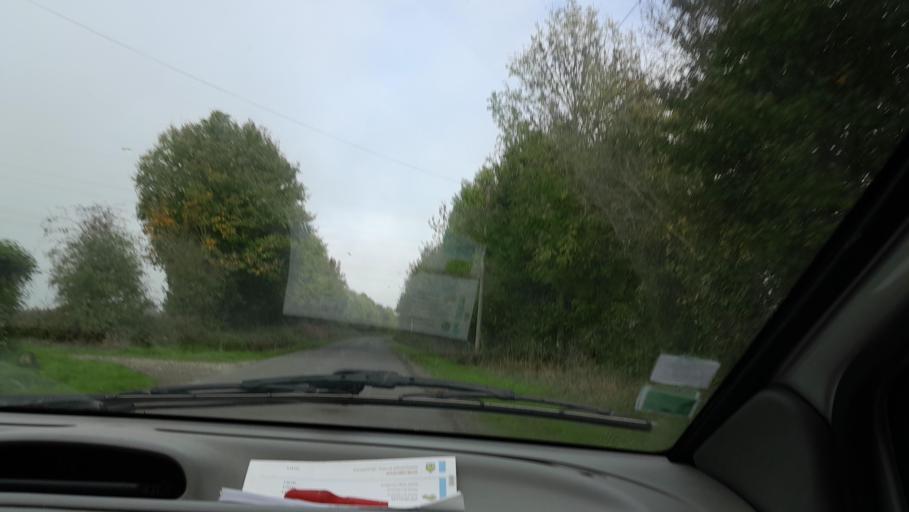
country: FR
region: Pays de la Loire
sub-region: Departement de la Mayenne
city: Saint-Pierre-la-Cour
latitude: 48.1460
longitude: -1.0318
